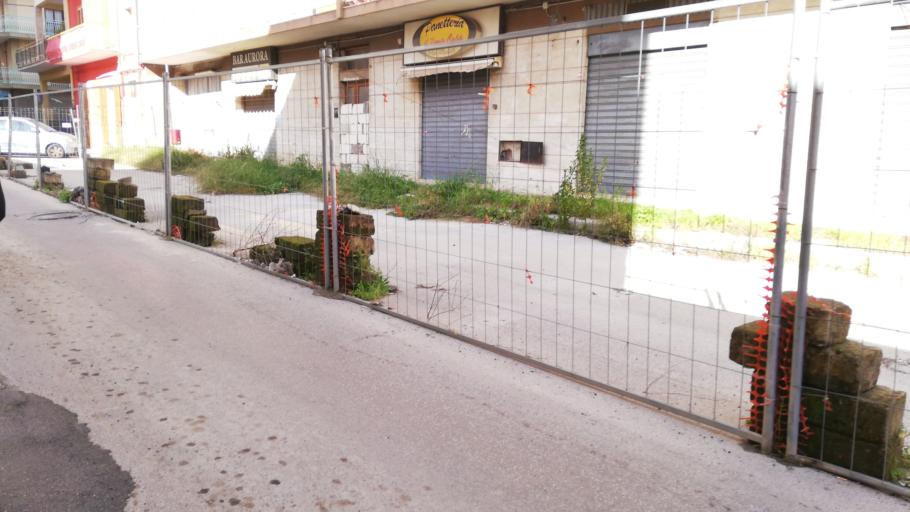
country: IT
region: Apulia
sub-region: Provincia di Bari
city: Bitonto
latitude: 41.1101
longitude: 16.6834
